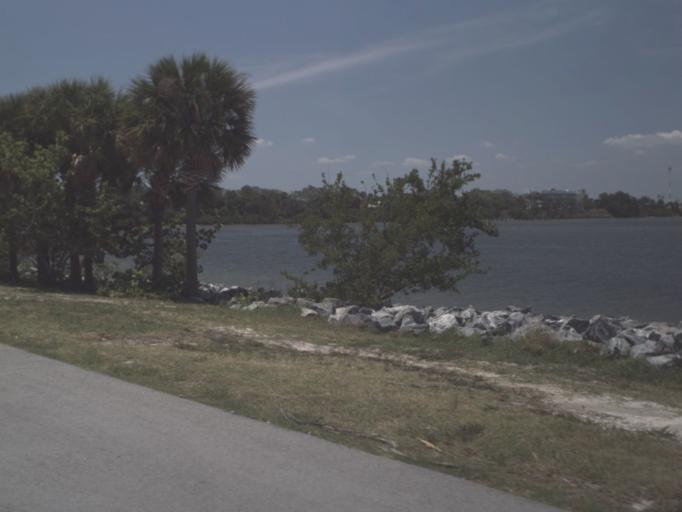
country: US
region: Florida
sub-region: Brevard County
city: Melbourne
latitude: 28.0820
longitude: -80.5978
